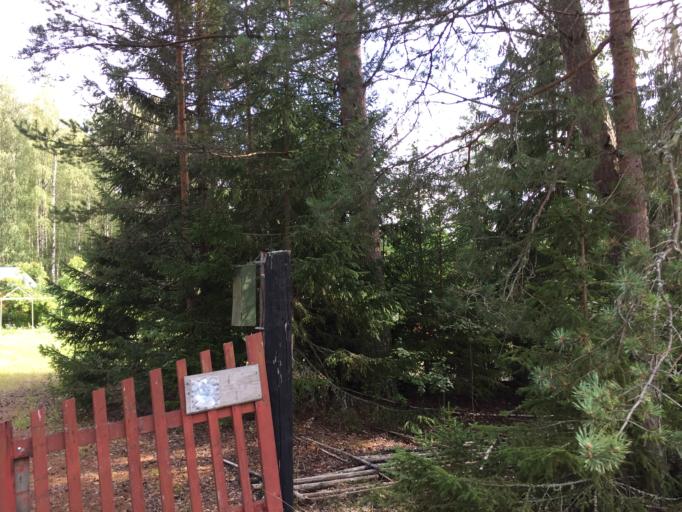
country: SE
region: Gaevleborg
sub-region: Ljusdals Kommun
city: Ljusdal
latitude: 61.8219
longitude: 16.0085
